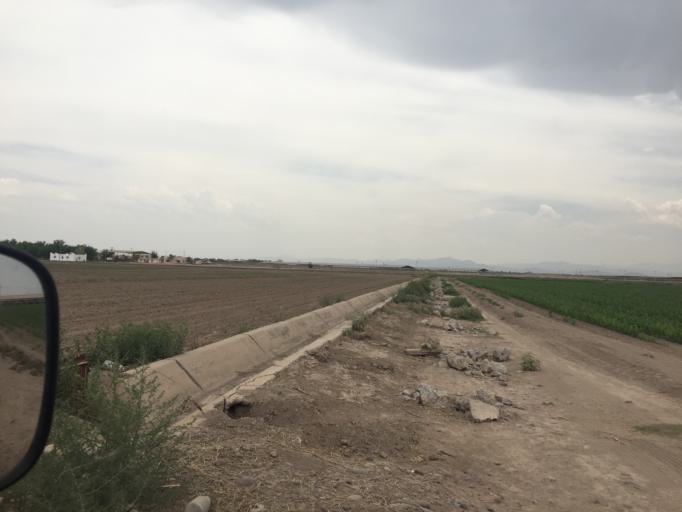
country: MX
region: Durango
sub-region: Gomez Palacio
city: San Jose de Vinedo
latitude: 25.6656
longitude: -103.4341
